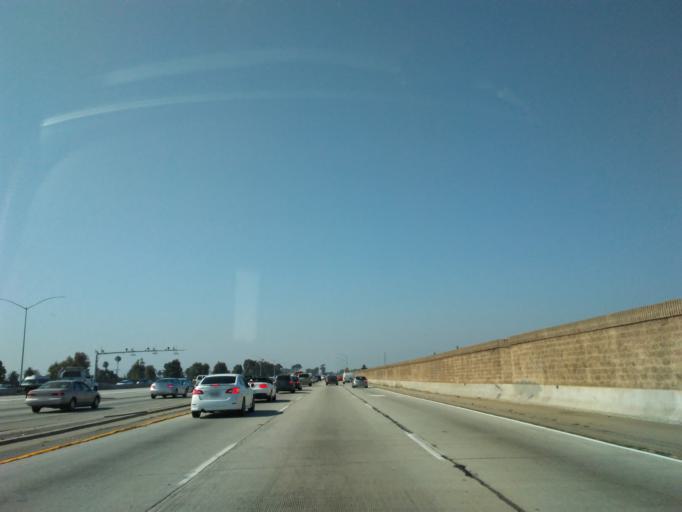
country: US
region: California
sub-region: Los Angeles County
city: Westmont
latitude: 33.9385
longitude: -118.2795
